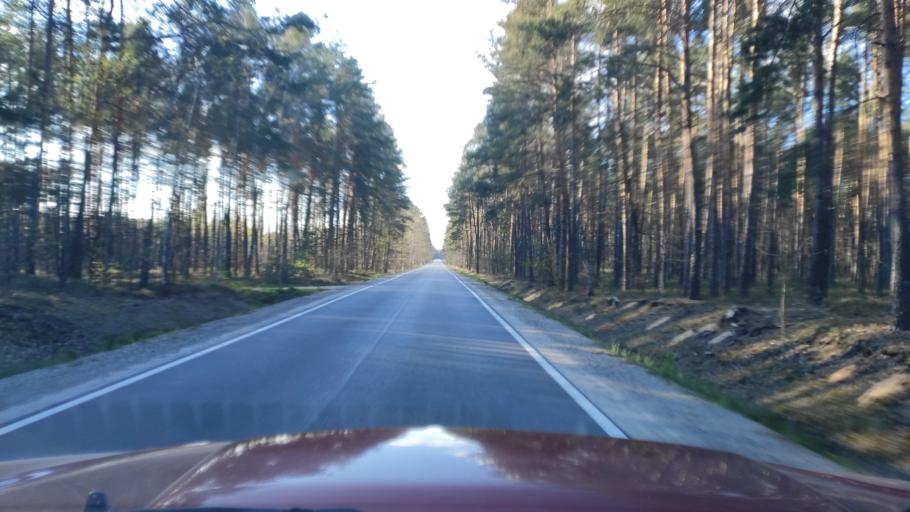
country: PL
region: Masovian Voivodeship
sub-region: Powiat zwolenski
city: Zwolen
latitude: 51.3909
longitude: 21.5489
